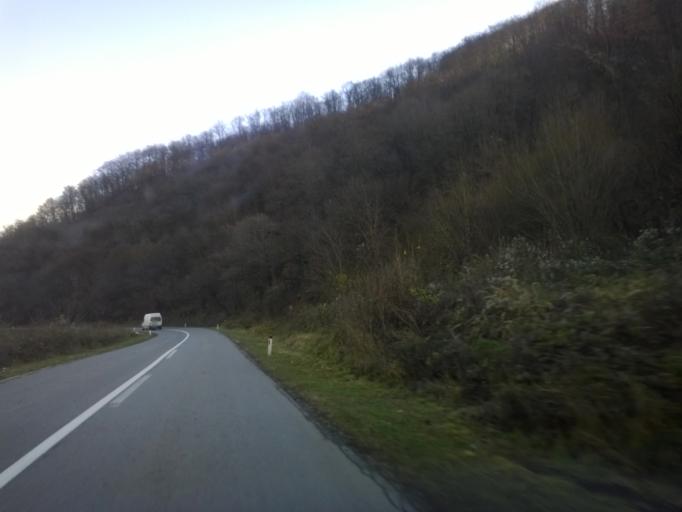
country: RO
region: Caras-Severin
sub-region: Comuna Pescari
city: Coronini
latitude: 44.6540
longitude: 21.7522
